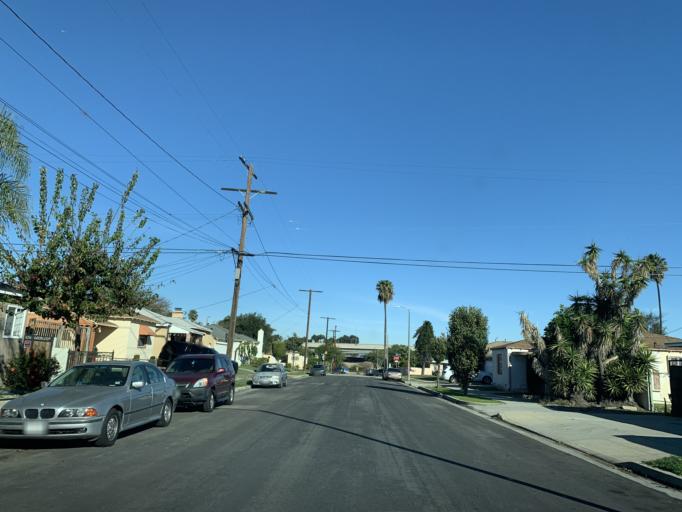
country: US
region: California
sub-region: Los Angeles County
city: West Athens
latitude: 33.9254
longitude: -118.2848
